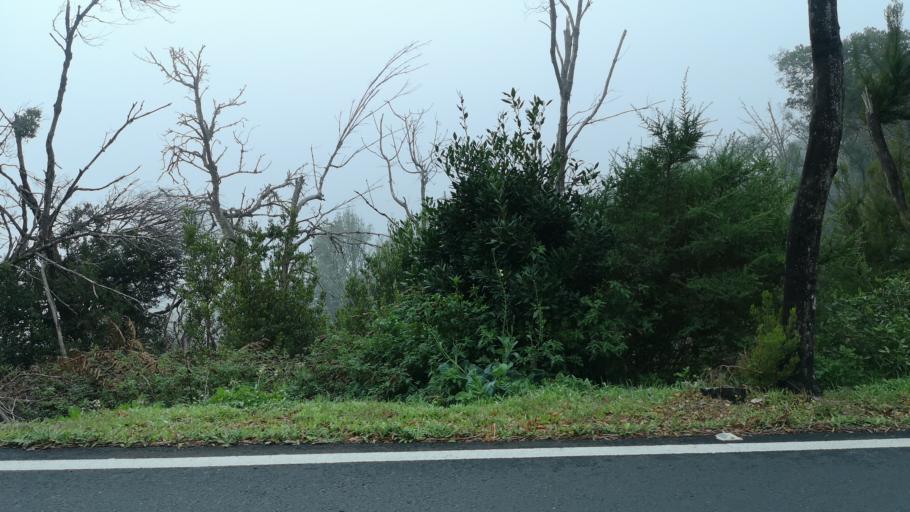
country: ES
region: Canary Islands
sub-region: Provincia de Santa Cruz de Tenerife
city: Vallehermosa
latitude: 28.1288
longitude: -17.2707
